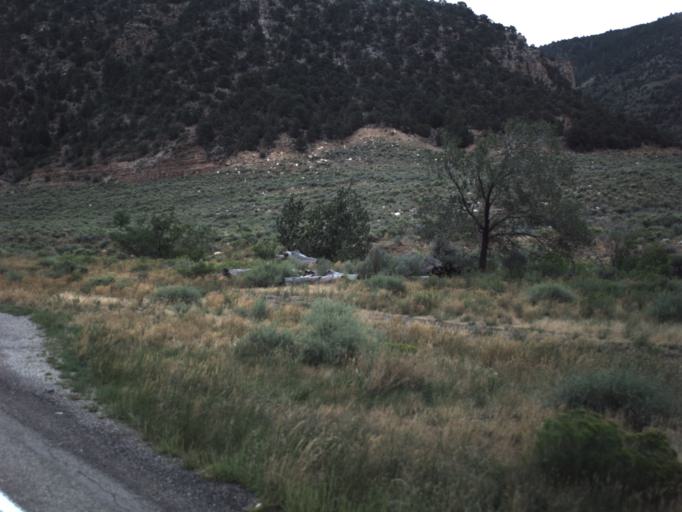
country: US
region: Utah
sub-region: Carbon County
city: East Carbon City
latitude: 39.5595
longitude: -110.3770
